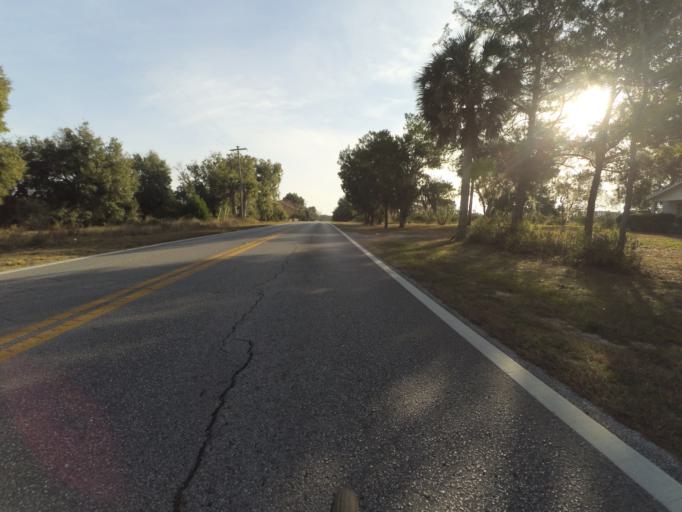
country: US
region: Florida
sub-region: Lake County
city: Umatilla
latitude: 28.9350
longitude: -81.6505
